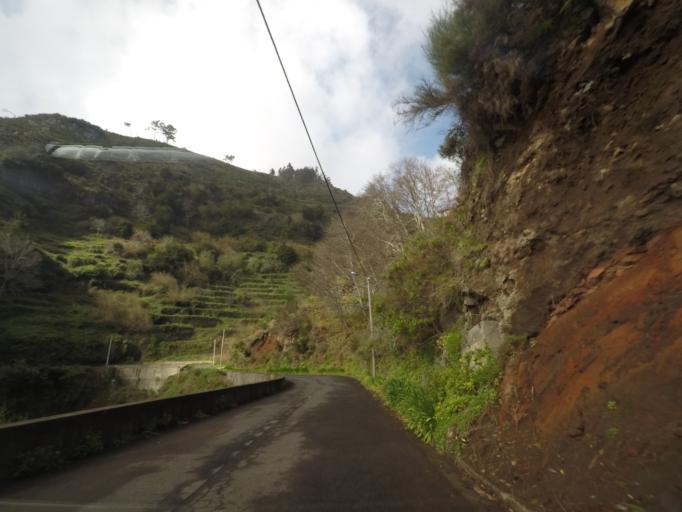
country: PT
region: Madeira
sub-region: Ribeira Brava
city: Campanario
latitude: 32.7033
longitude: -17.0241
